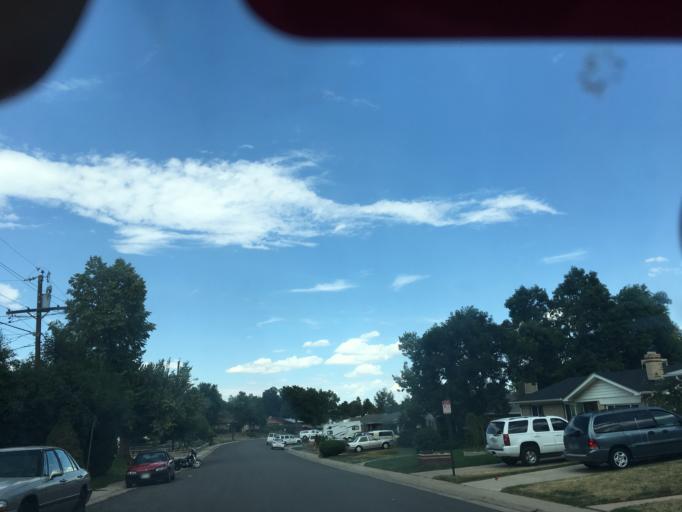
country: US
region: Colorado
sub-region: Jefferson County
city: Lakewood
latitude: 39.6843
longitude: -105.0530
